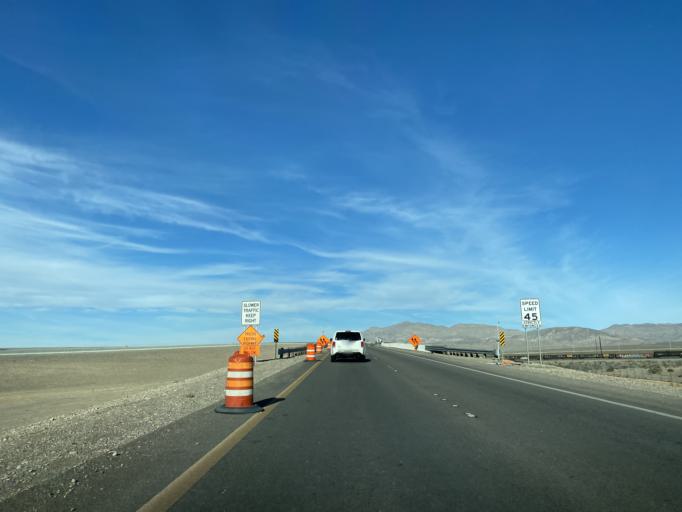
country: US
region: Nevada
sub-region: Clark County
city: Nellis Air Force Base
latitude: 36.2780
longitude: -115.0611
